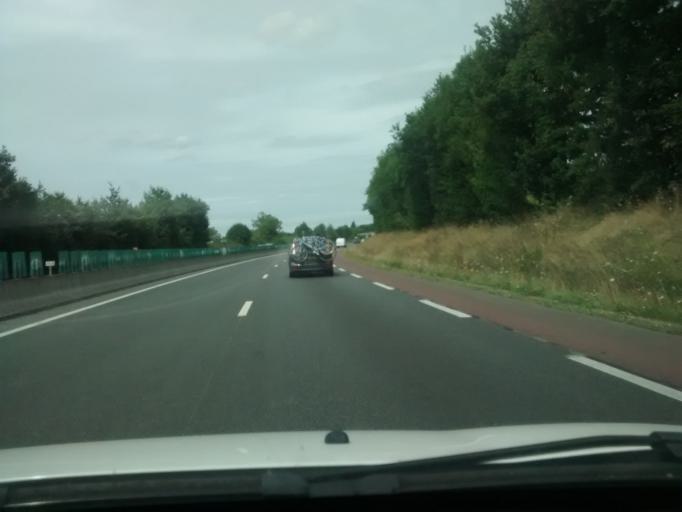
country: FR
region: Lower Normandy
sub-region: Departement de la Manche
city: Le Val-Saint-Pere
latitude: 48.6595
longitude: -1.3638
